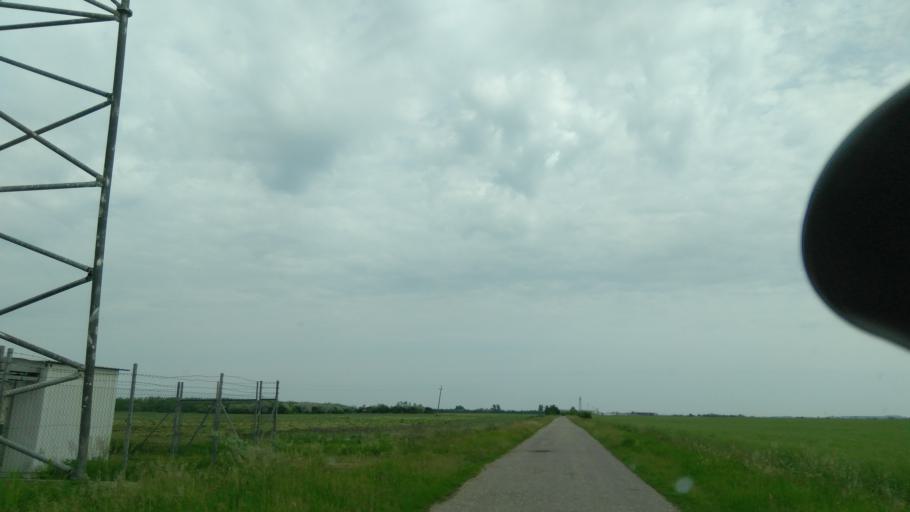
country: HU
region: Bekes
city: Szeghalom
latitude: 47.0383
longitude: 21.1542
